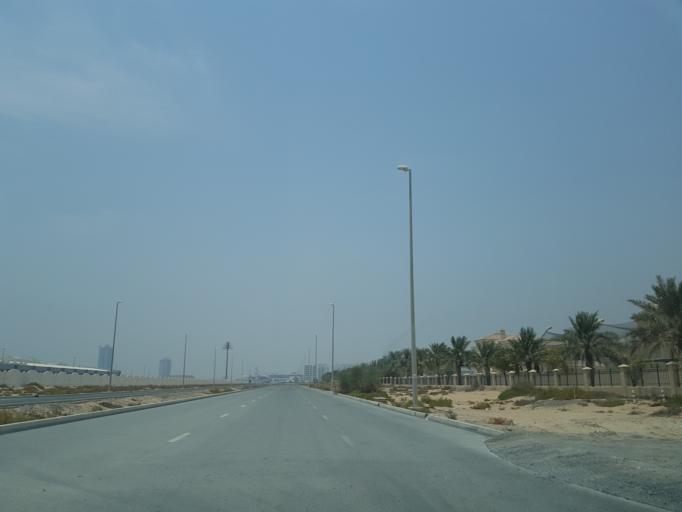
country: AE
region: Dubai
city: Dubai
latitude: 25.0318
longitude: 55.2500
